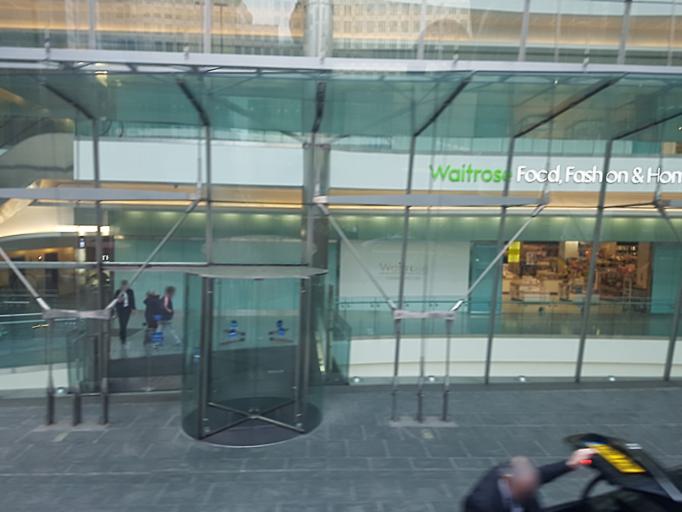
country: GB
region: England
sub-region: Greater London
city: Poplar
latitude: 51.5048
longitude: -0.0173
